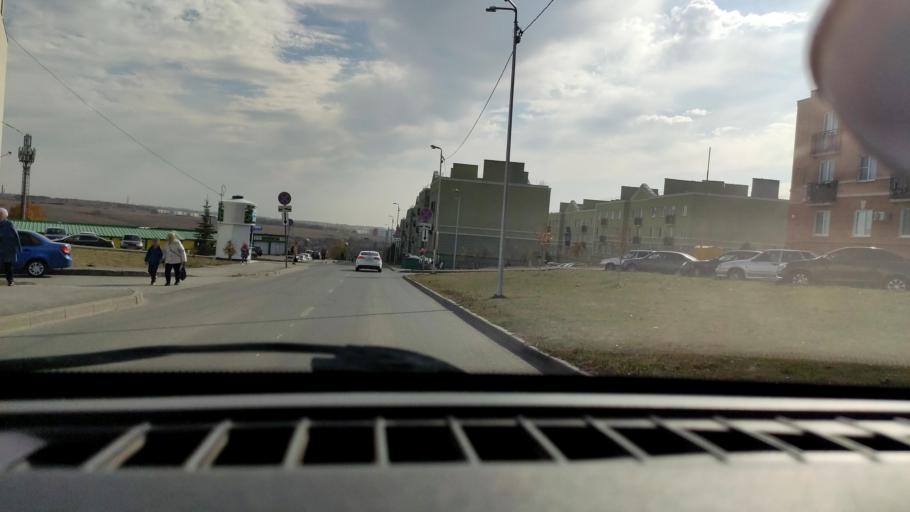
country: RU
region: Samara
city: Petra-Dubrava
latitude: 53.3208
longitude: 50.3133
